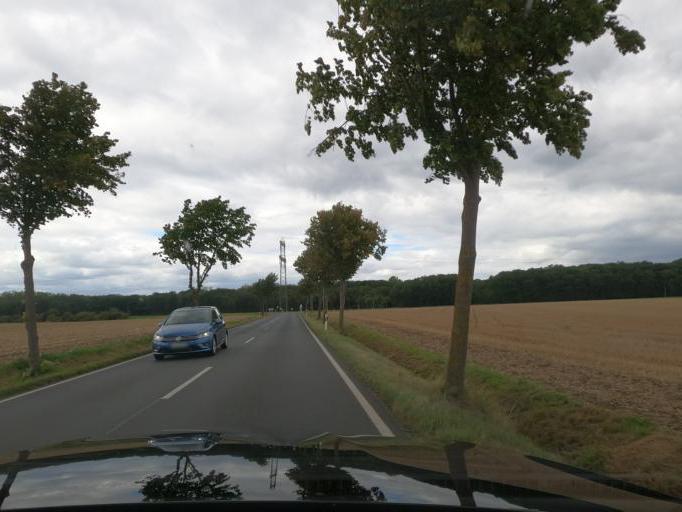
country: DE
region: Lower Saxony
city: Sehnde
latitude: 52.3022
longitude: 9.8996
